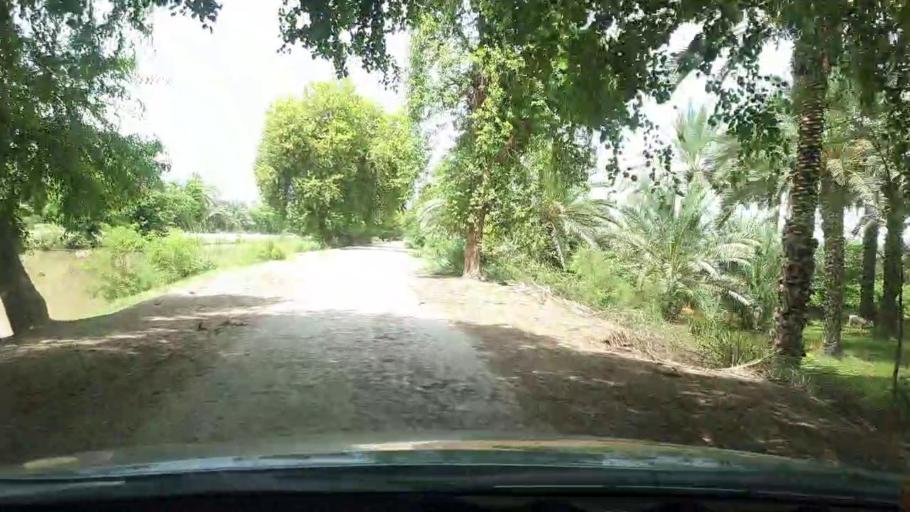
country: PK
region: Sindh
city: Khairpur
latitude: 27.4651
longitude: 68.8046
